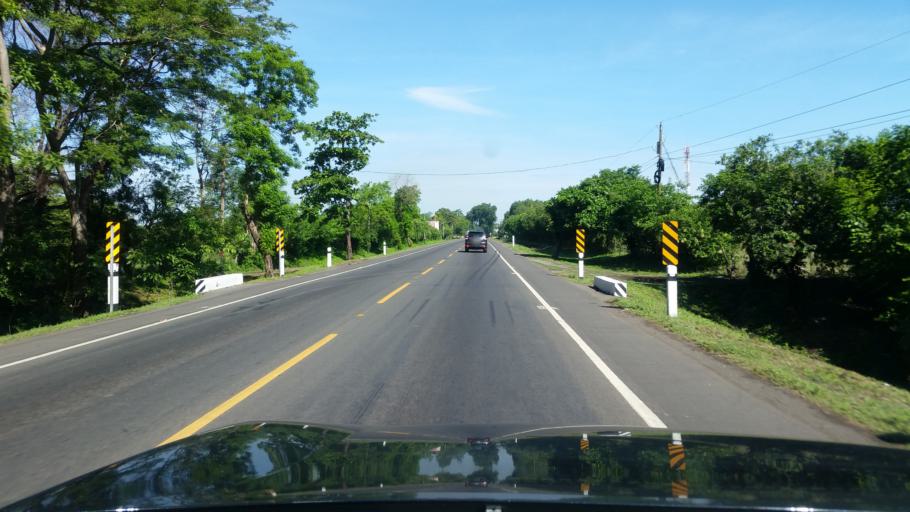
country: NI
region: Chinandega
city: Chinandega
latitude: 12.6129
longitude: -87.0885
